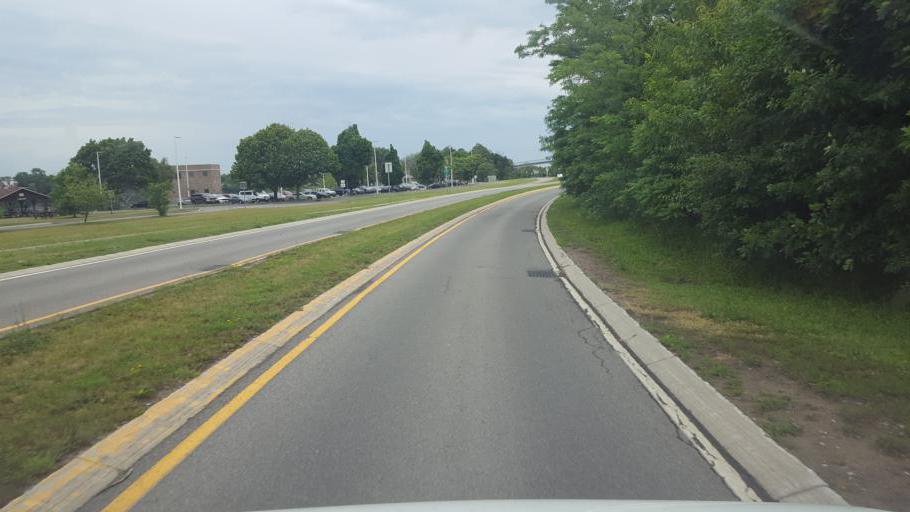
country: US
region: New York
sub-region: Niagara County
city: Niagara Falls
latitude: 43.0910
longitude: -79.0620
